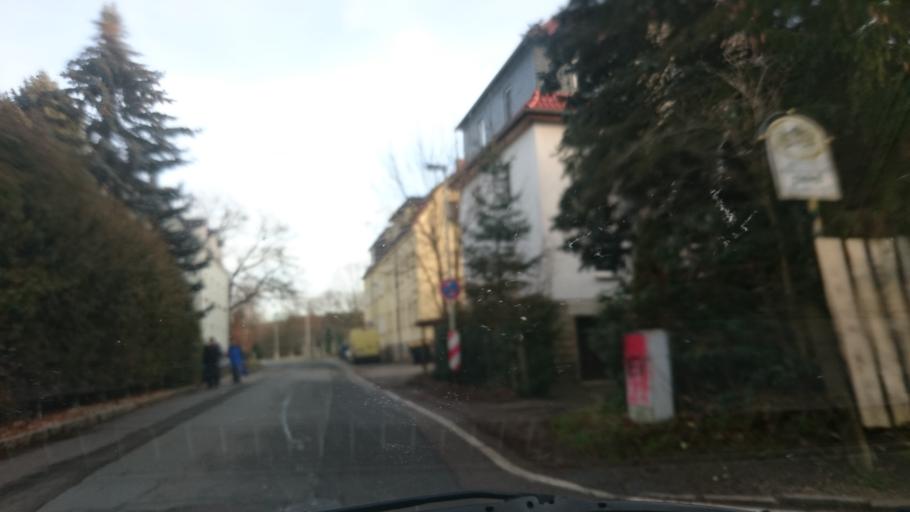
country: DE
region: Saxony
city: Zwickau
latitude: 50.7385
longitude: 12.5183
